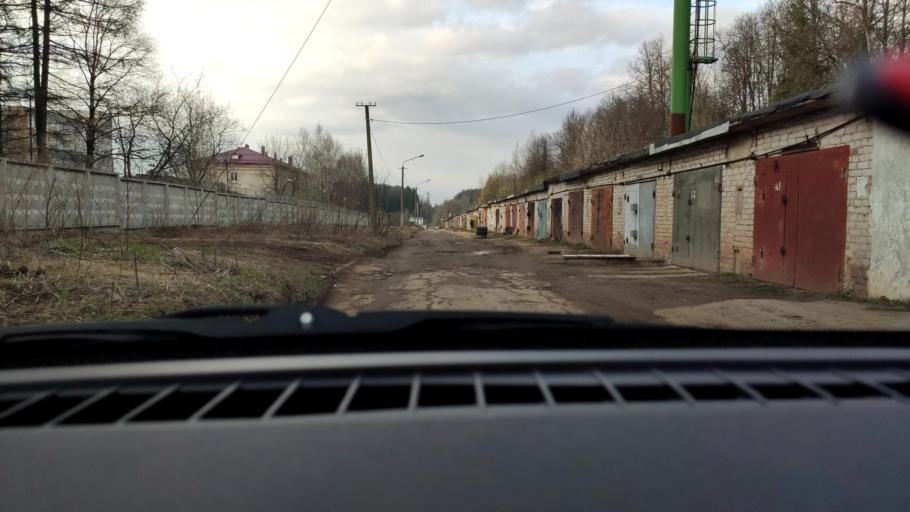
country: RU
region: Perm
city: Froly
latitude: 57.9733
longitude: 56.3215
